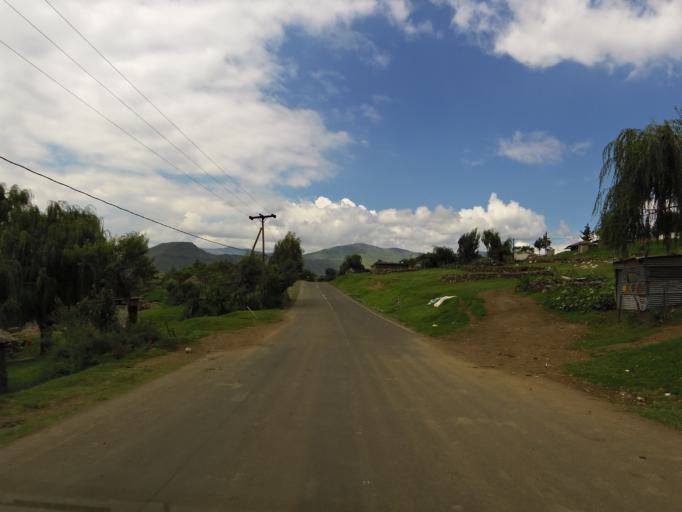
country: LS
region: Butha-Buthe
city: Butha-Buthe
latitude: -29.1084
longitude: 28.4860
